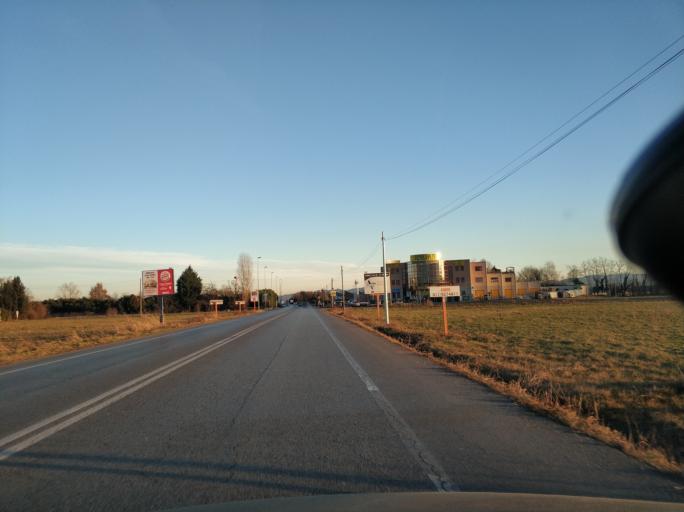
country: IT
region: Piedmont
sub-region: Provincia di Torino
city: Caselle Torinese
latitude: 45.1926
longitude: 7.6303
